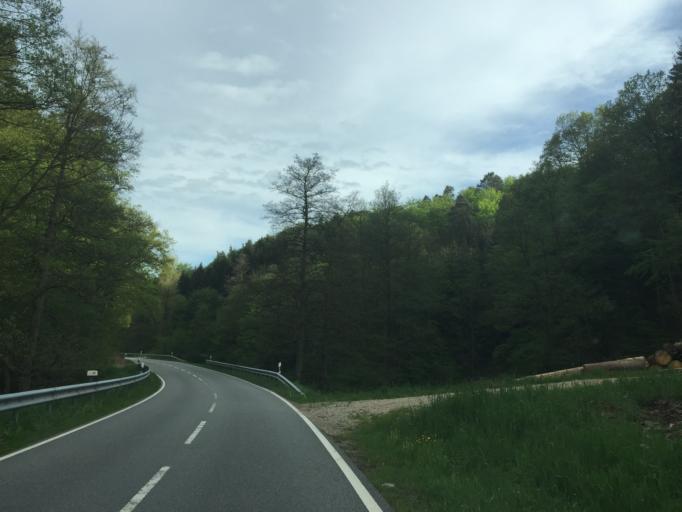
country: DE
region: Baden-Wuerttemberg
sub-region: Karlsruhe Region
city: Wilhelmsfeld
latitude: 49.4857
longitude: 8.7250
